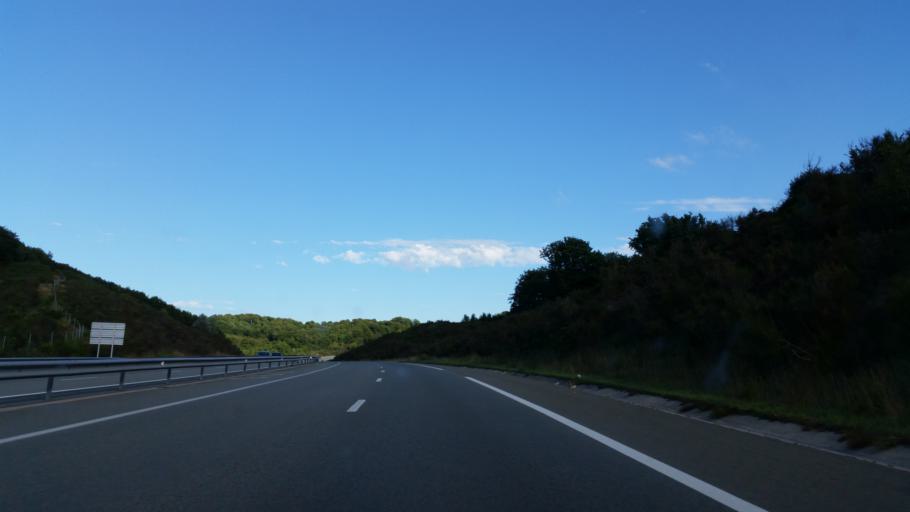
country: FR
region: Franche-Comte
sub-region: Departement de la Haute-Saone
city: Ronchamp
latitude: 47.6202
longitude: 6.6644
